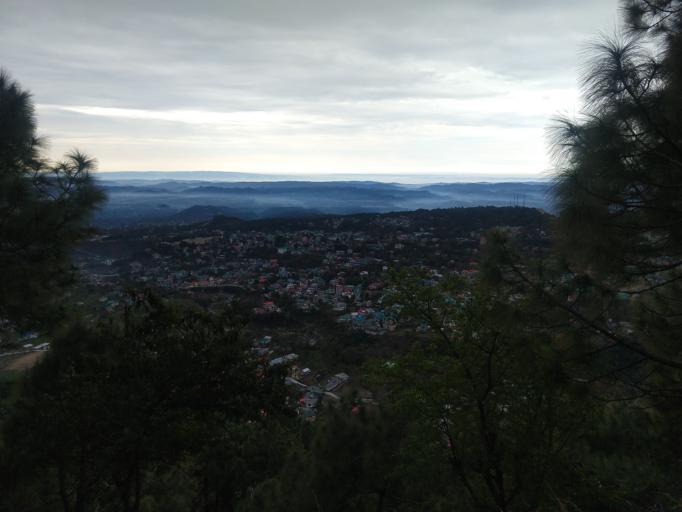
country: IN
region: Himachal Pradesh
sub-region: Kangra
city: Dharmsala
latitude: 32.2191
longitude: 76.3345
